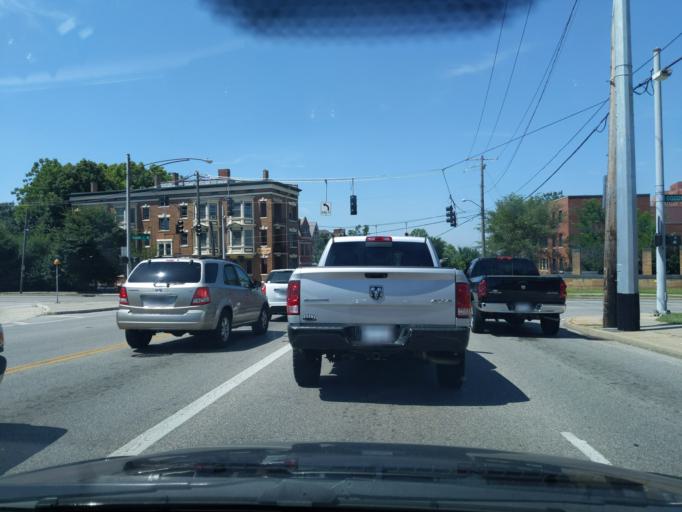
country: US
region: Ohio
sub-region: Hamilton County
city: Saint Bernard
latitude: 39.1375
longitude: -84.5094
